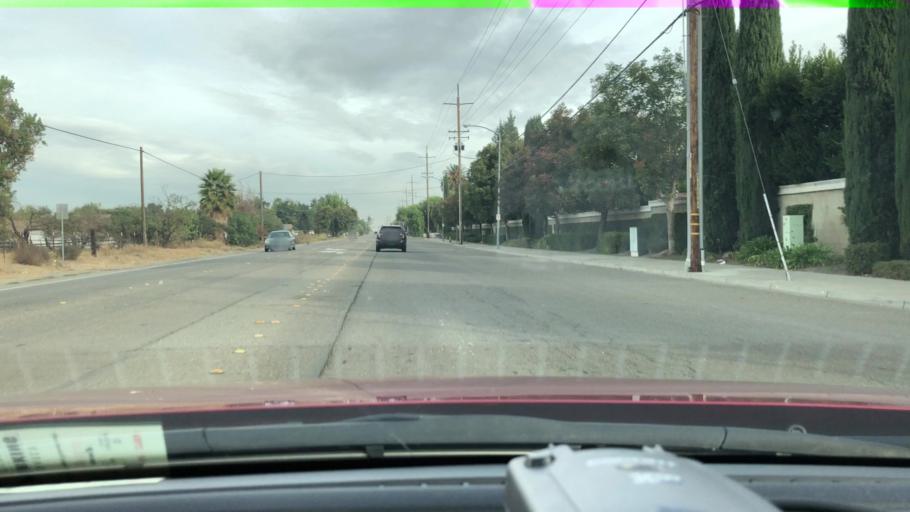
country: US
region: California
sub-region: San Joaquin County
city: Lathrop
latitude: 37.8195
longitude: -121.2534
